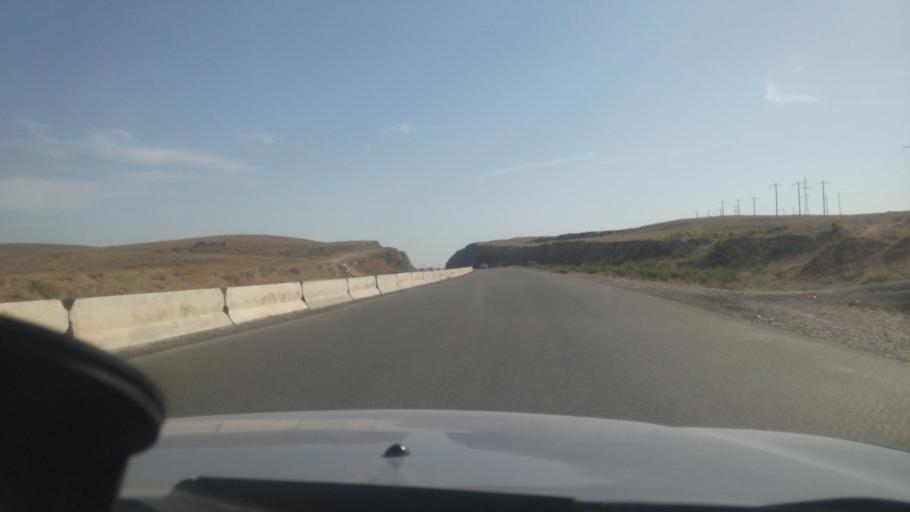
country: UZ
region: Jizzax
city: Jizzax
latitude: 40.0464
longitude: 67.6737
